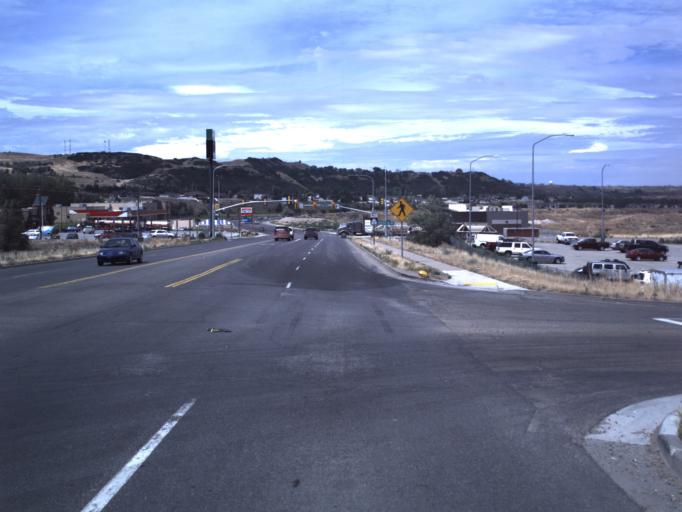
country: US
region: Utah
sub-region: Weber County
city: Uintah
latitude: 41.1281
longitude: -111.9089
